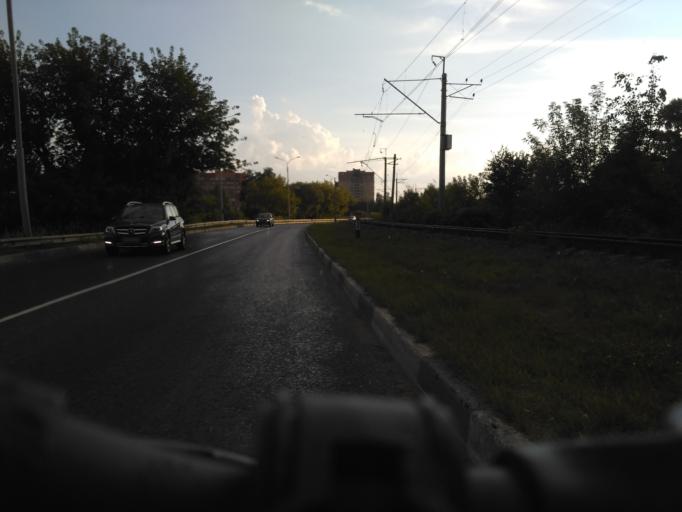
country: RU
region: Moskovskaya
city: Dubna
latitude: 56.7385
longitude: 37.1576
